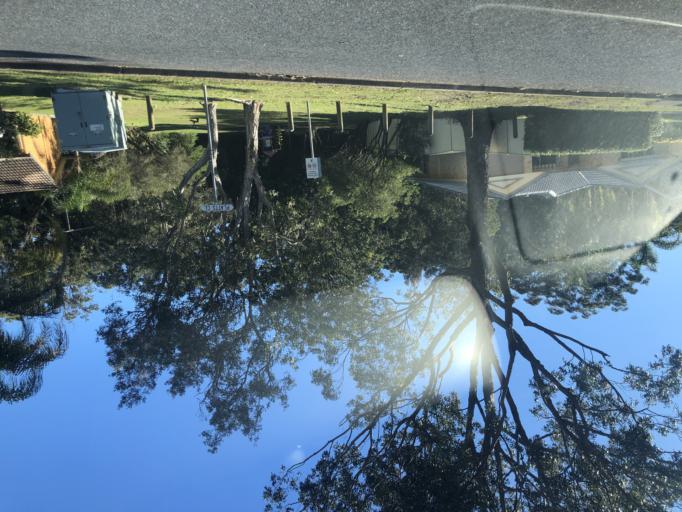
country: AU
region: New South Wales
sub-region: Coffs Harbour
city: Toormina
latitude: -30.3671
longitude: 153.0847
